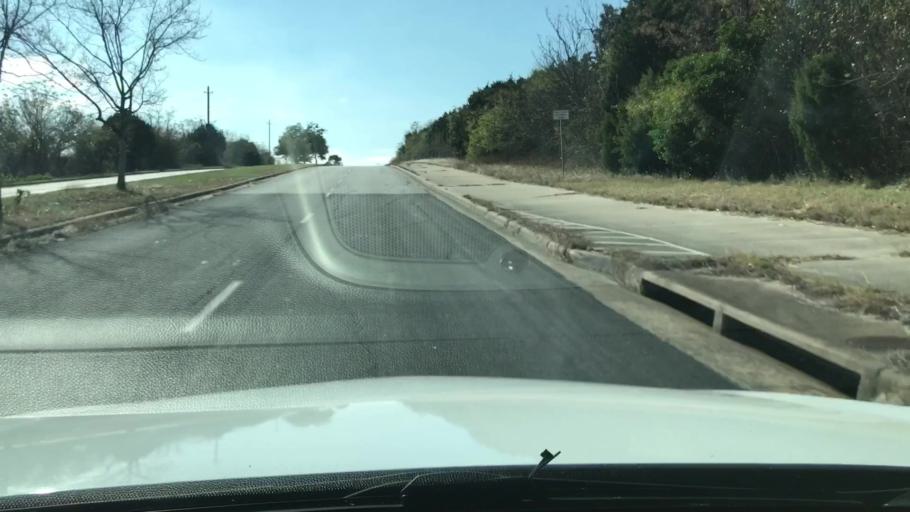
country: US
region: Texas
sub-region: Travis County
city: Onion Creek
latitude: 30.1760
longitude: -97.7217
